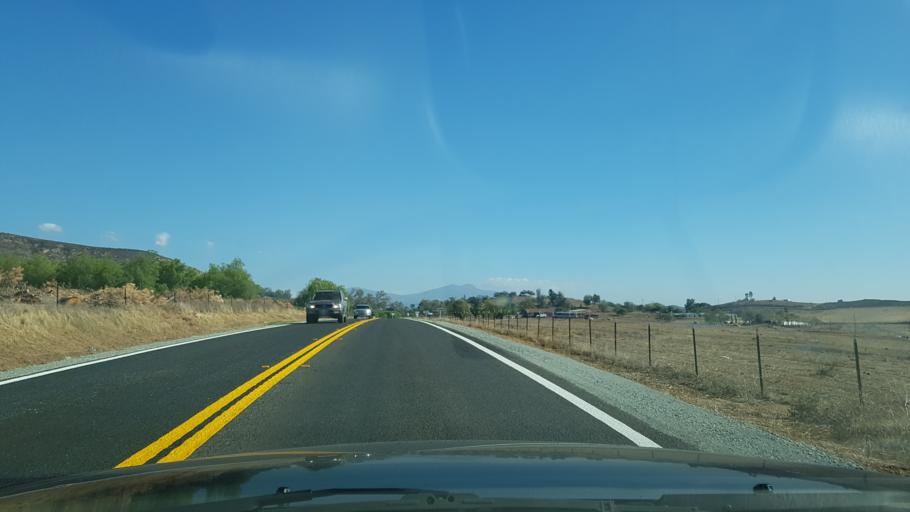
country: US
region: California
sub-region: San Diego County
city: San Diego Country Estates
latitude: 33.0777
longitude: -116.7764
